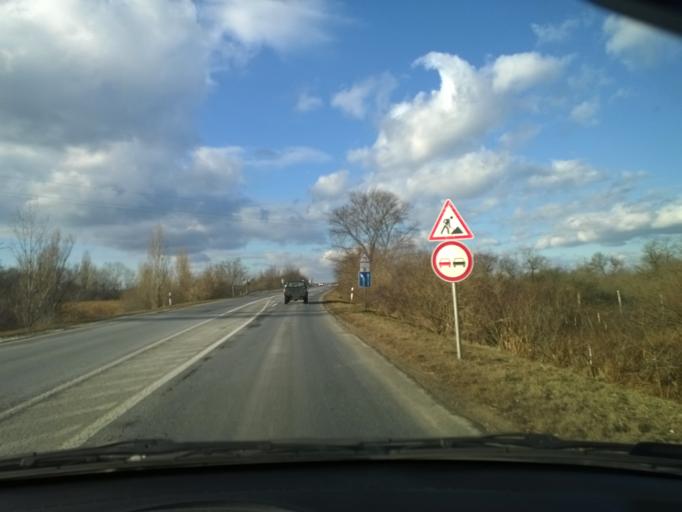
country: HU
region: Fejer
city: Pakozd
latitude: 47.1906
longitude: 18.5123
